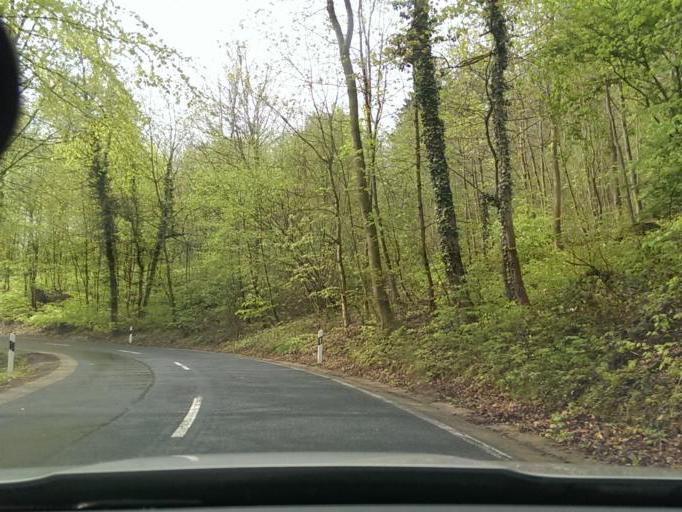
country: DE
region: Lower Saxony
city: Nordstemmen
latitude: 52.1763
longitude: 9.7652
